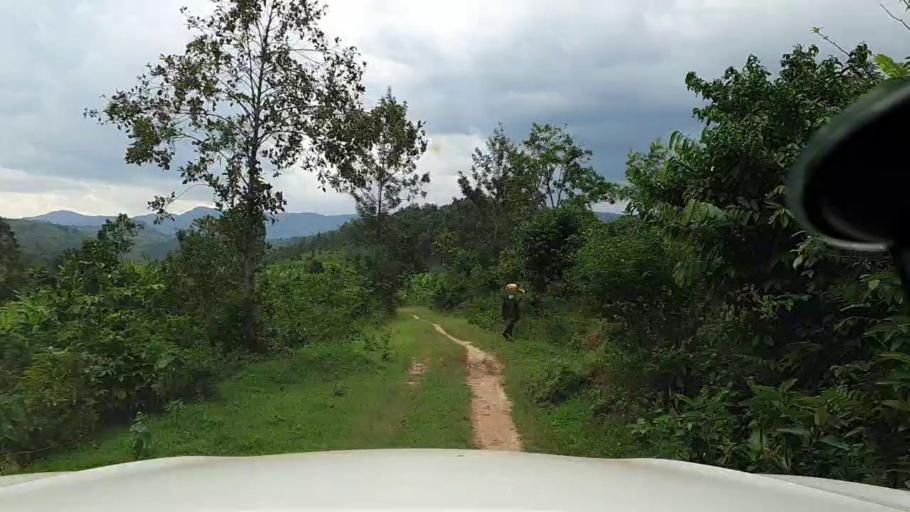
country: RW
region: Southern Province
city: Gitarama
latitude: -1.8140
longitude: 29.8012
